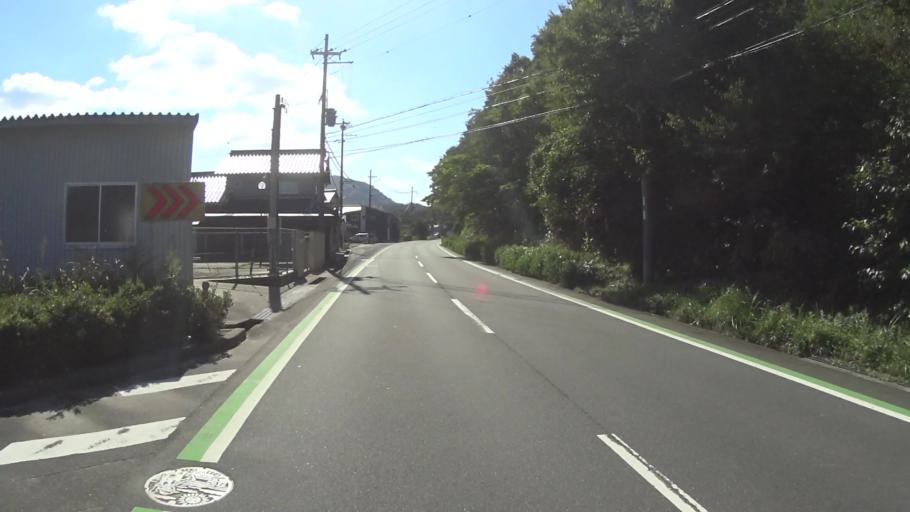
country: JP
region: Kyoto
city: Miyazu
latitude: 35.6547
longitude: 135.0896
